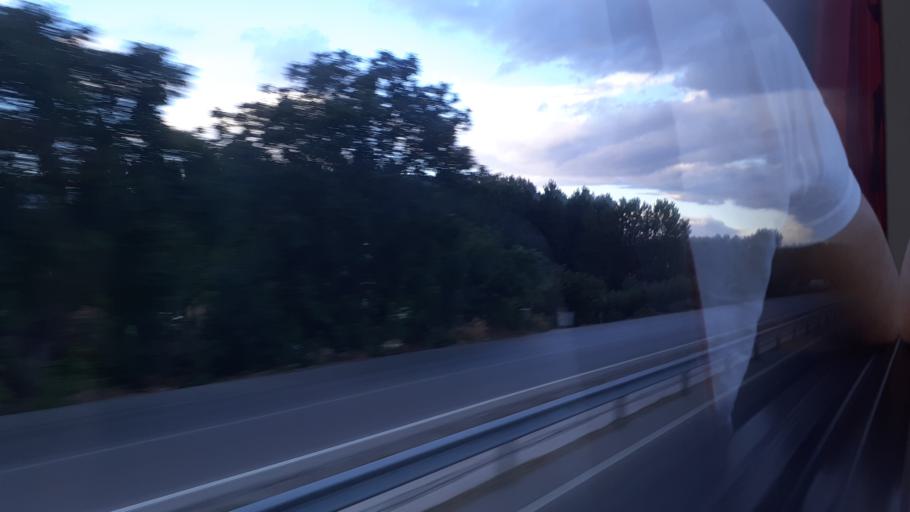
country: TR
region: Tokat
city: Dokmetepe
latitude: 40.3218
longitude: 36.2117
